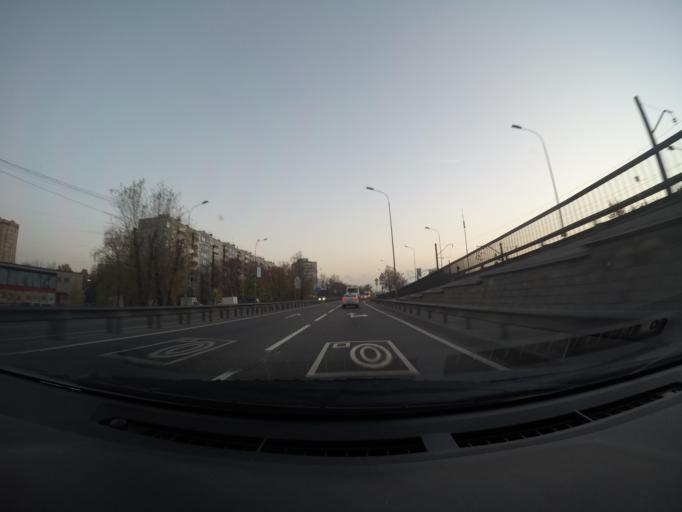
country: RU
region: Moskovskaya
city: Lyubertsy
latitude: 55.6675
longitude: 37.8838
